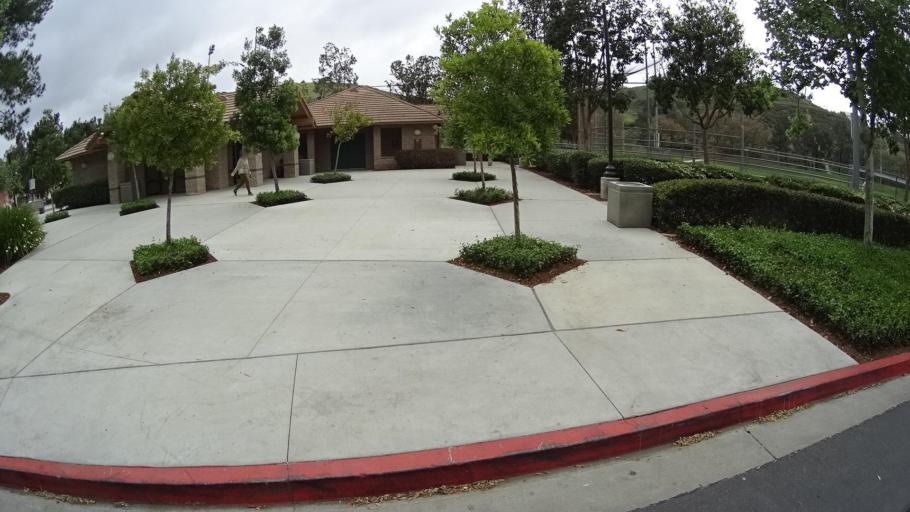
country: US
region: California
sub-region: Los Angeles County
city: Diamond Bar
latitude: 34.0141
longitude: -117.7914
